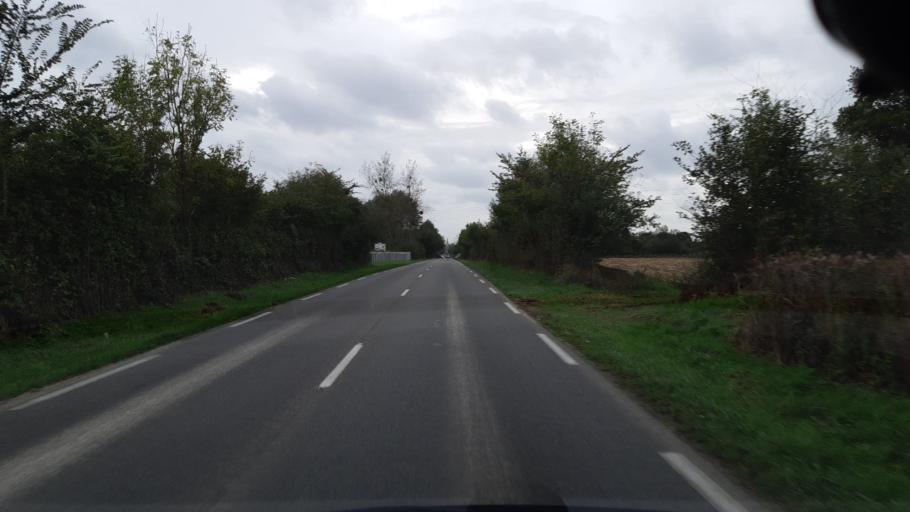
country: FR
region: Lower Normandy
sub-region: Departement de la Manche
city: Brehal
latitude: 48.9049
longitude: -1.4840
